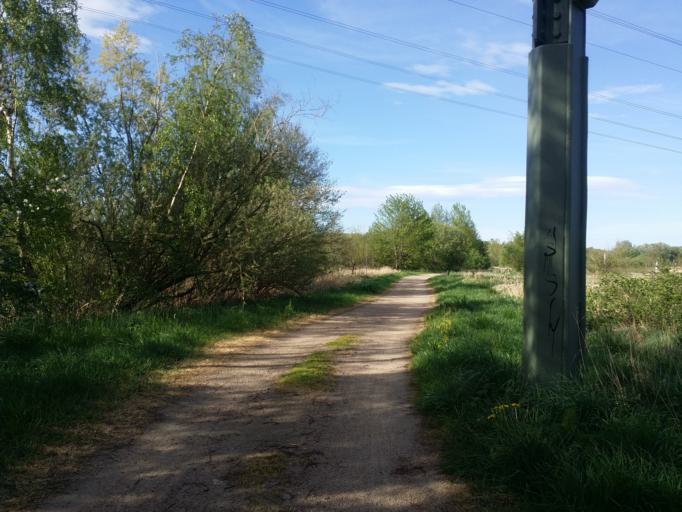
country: DE
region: Lower Saxony
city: Lemwerder
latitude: 53.1518
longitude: 8.6700
